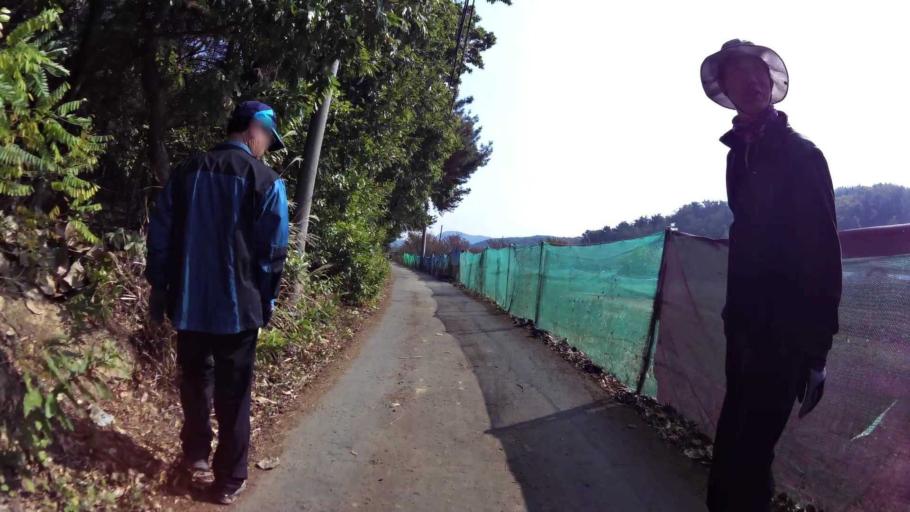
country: KR
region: Daegu
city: Daegu
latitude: 35.8595
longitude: 128.6674
